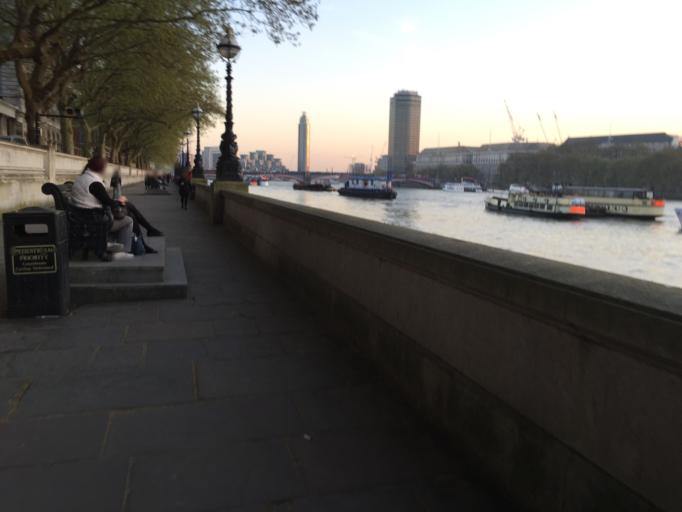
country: GB
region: England
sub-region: Greater London
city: City of Westminster
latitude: 51.4984
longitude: -0.1204
